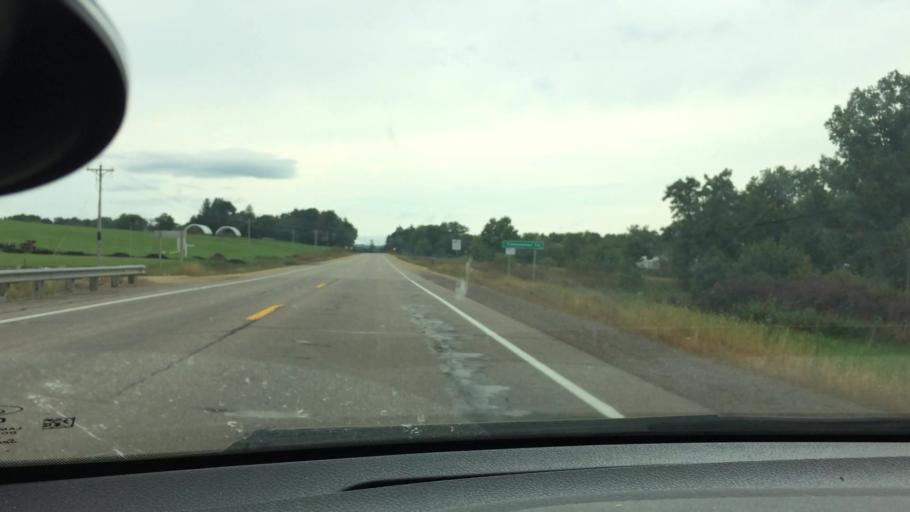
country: US
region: Wisconsin
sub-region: Trempealeau County
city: Osseo
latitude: 44.5891
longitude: -91.1651
